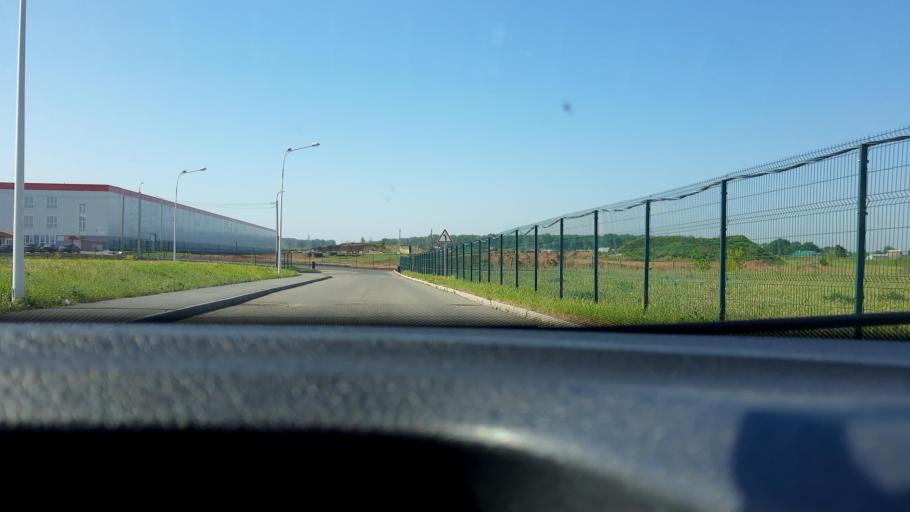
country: RU
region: Bashkortostan
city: Ufa
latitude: 54.6028
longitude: 55.9020
